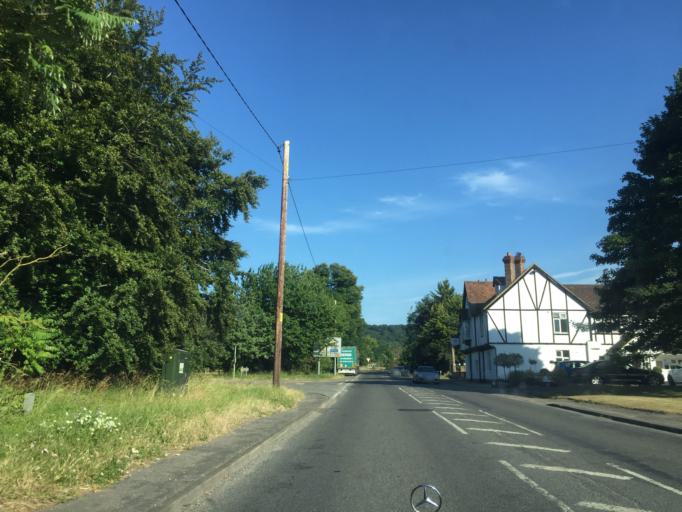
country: GB
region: England
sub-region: Oxfordshire
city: Chinnor
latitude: 51.6781
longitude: -0.9558
